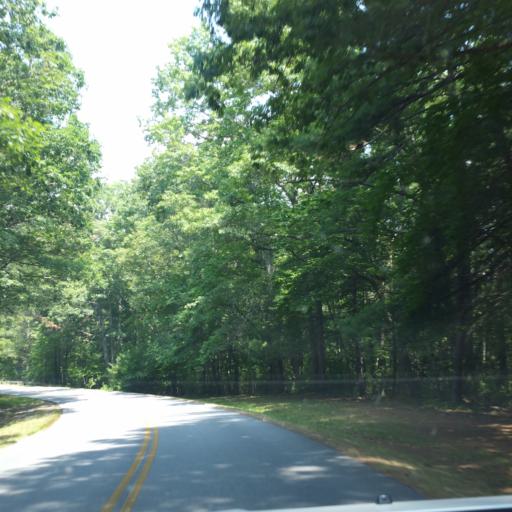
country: US
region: North Carolina
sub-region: Buncombe County
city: Bent Creek
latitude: 35.5004
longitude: -82.5783
